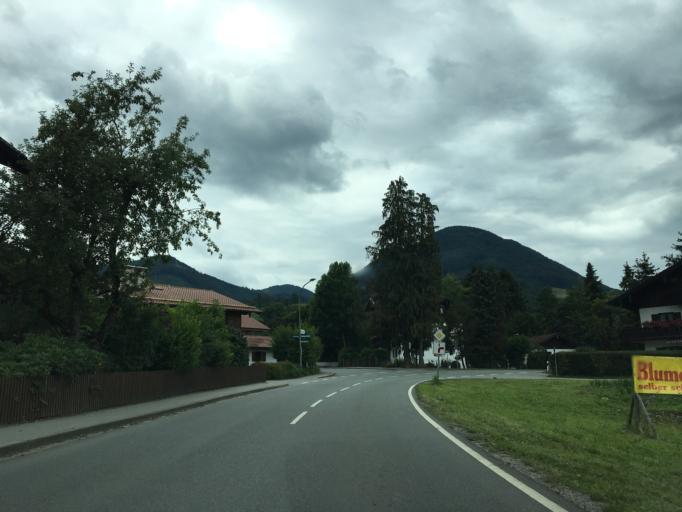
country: DE
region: Bavaria
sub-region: Upper Bavaria
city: Brannenburg
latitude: 47.7409
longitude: 12.0955
